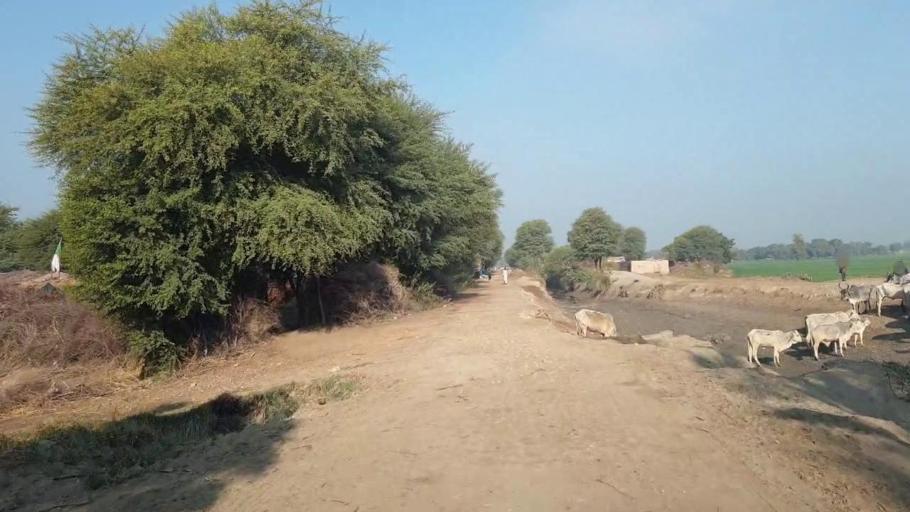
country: PK
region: Sindh
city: Shahdadpur
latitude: 25.9687
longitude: 68.6159
